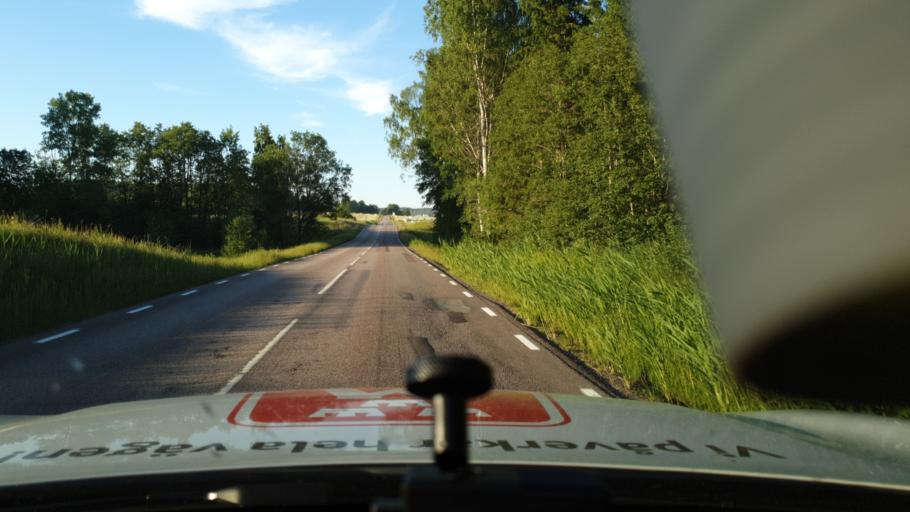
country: SE
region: Vaermland
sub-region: Kils Kommun
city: Kil
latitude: 59.5719
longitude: 13.2960
